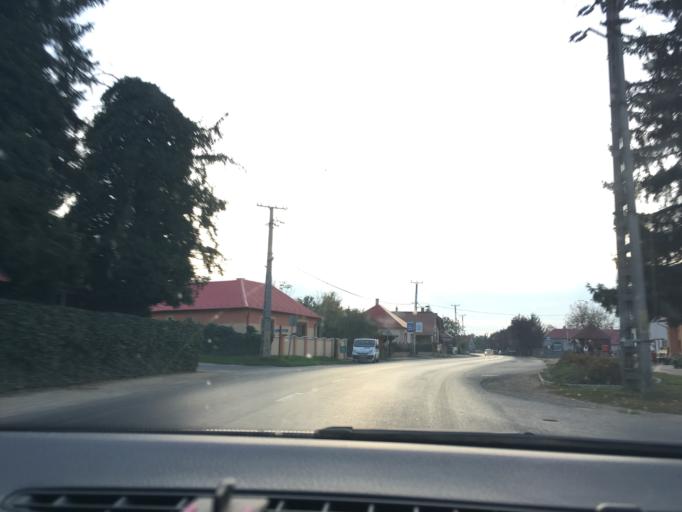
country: HU
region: Szabolcs-Szatmar-Bereg
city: Kallosemjen
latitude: 47.8592
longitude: 21.9236
